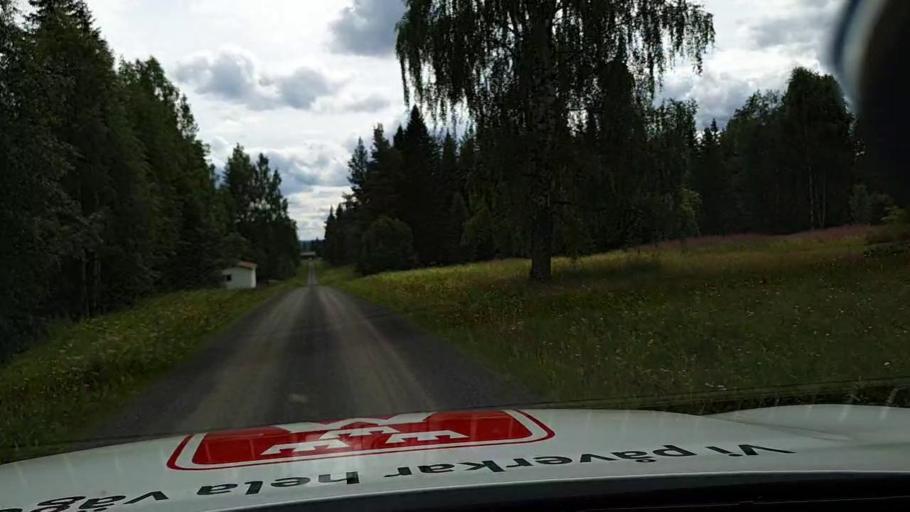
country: SE
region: Jaemtland
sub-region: OEstersunds Kommun
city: Lit
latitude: 63.2845
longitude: 15.2415
